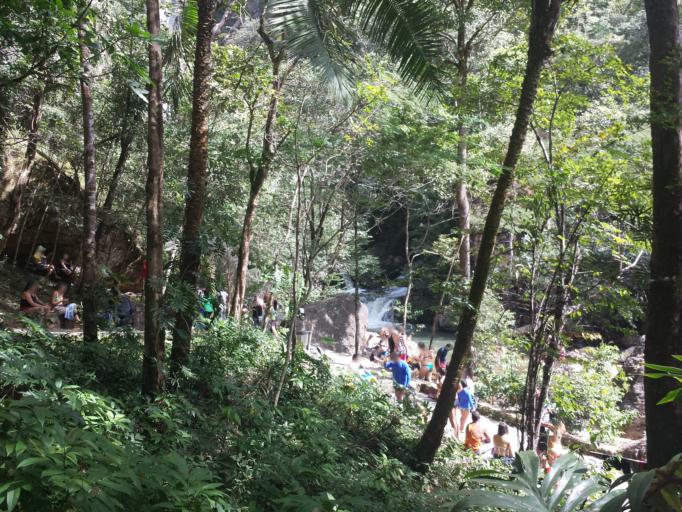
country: BR
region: Goias
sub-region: Planaltina
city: Planaltina
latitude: -15.3674
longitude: -47.4538
